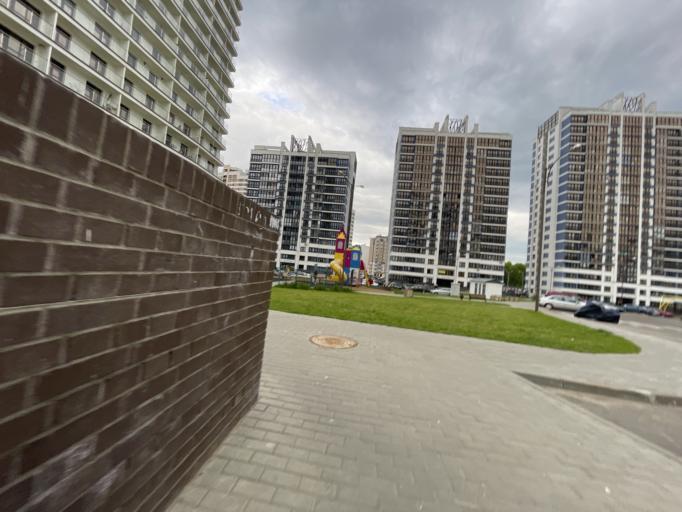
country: BY
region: Minsk
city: Minsk
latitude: 53.8710
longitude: 27.5520
